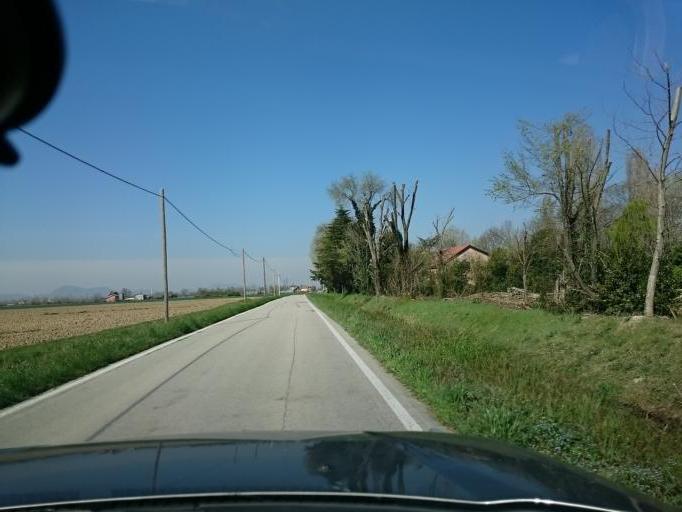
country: IT
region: Veneto
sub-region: Provincia di Padova
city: Ponte San Nicolo
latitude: 45.3447
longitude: 11.9255
